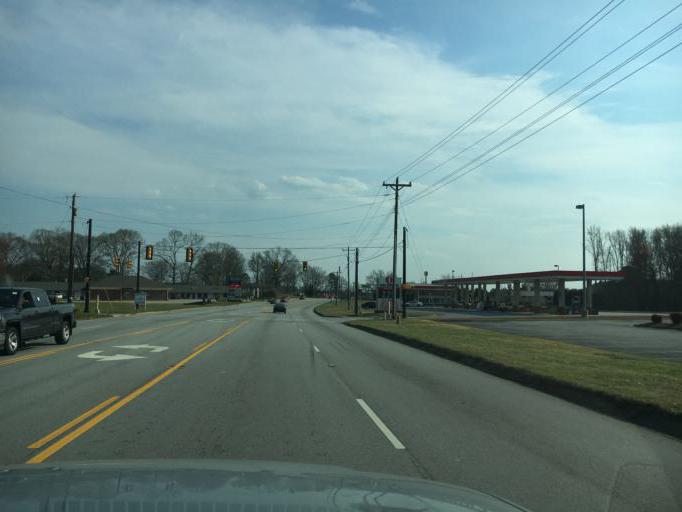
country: US
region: South Carolina
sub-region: Spartanburg County
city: Mayo
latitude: 35.0271
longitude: -81.8959
